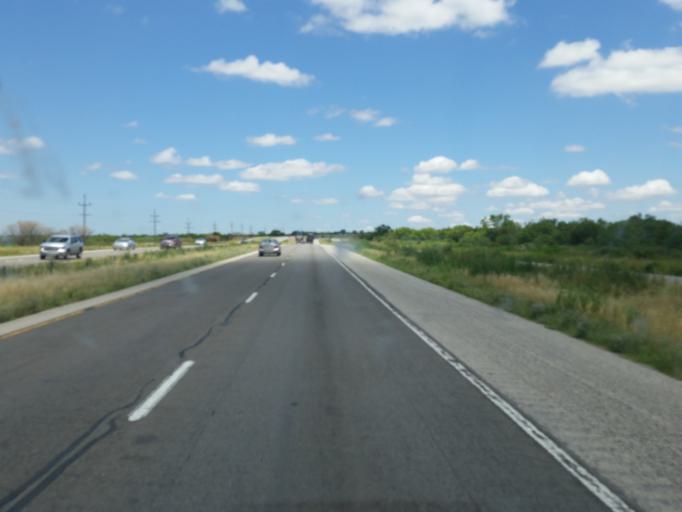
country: US
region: Texas
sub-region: Nolan County
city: Sweetwater
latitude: 32.4958
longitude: -100.2745
